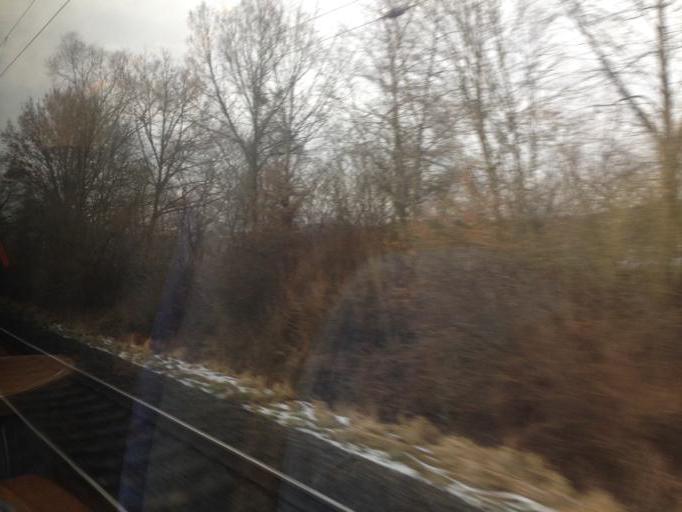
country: DE
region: Hesse
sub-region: Regierungsbezirk Giessen
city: Ehringshausen
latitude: 50.5931
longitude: 8.3918
